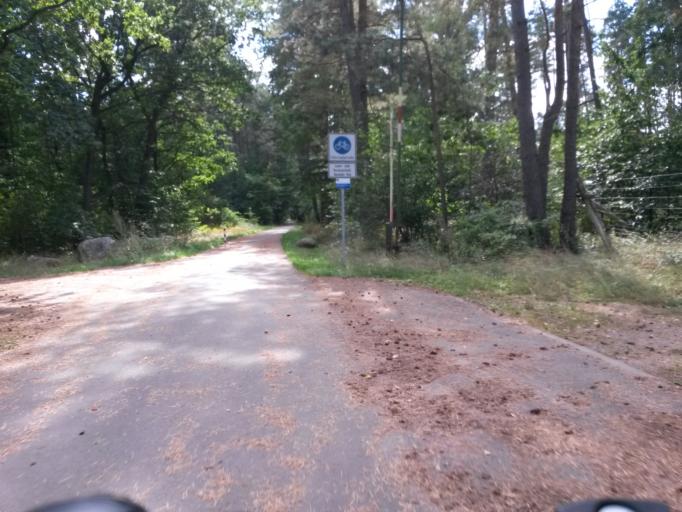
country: DE
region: Brandenburg
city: Templin
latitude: 53.1732
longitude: 13.5165
